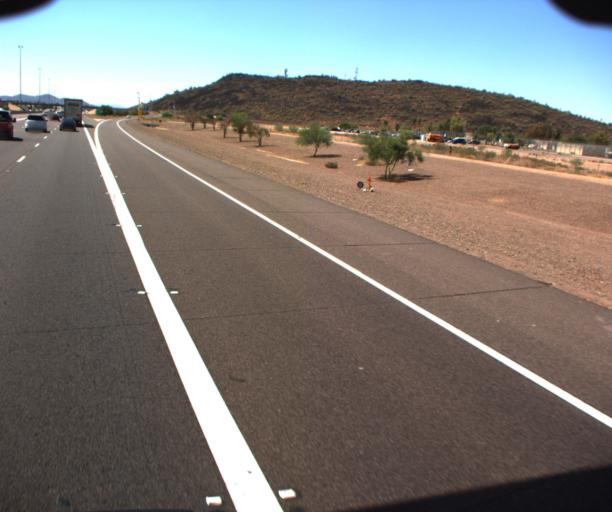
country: US
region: Arizona
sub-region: Maricopa County
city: Anthem
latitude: 33.7050
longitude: -112.1160
